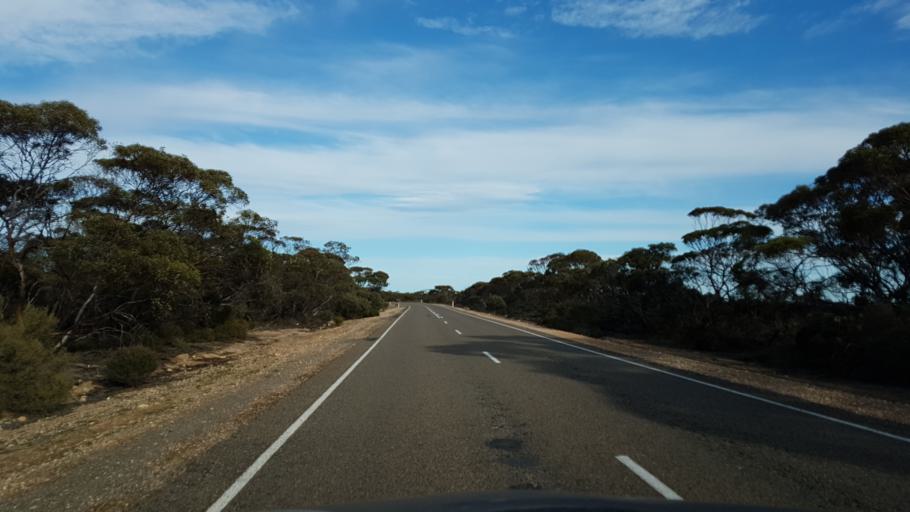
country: AU
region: South Australia
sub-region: Mid Murray
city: Mannum
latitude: -35.0114
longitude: 139.5148
